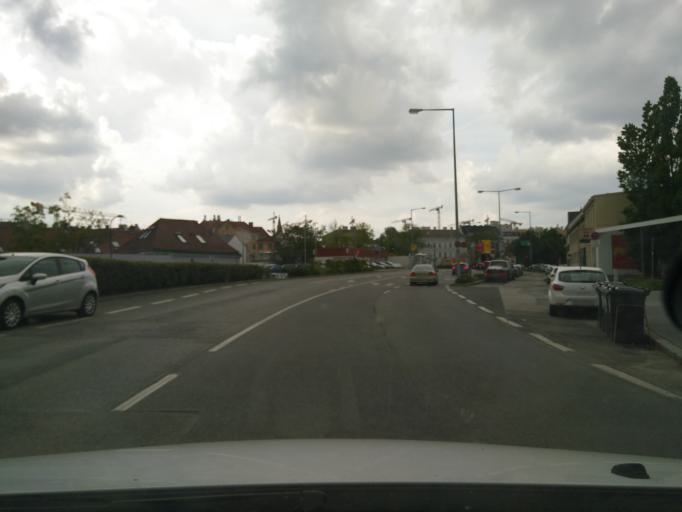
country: AT
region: Lower Austria
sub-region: Politischer Bezirk Modling
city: Brunn am Gebirge
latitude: 48.1450
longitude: 16.2974
